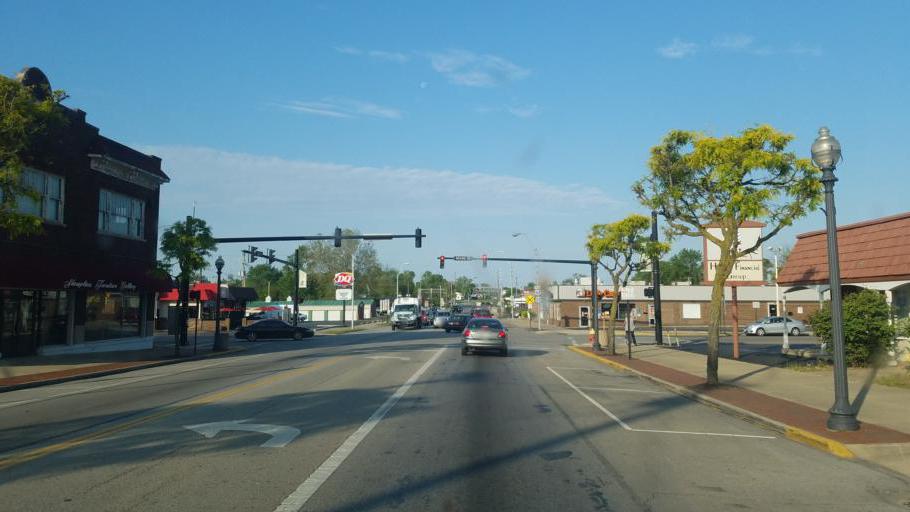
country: US
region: Ohio
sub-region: Fayette County
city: Washington Court House
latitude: 39.5353
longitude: -83.4407
